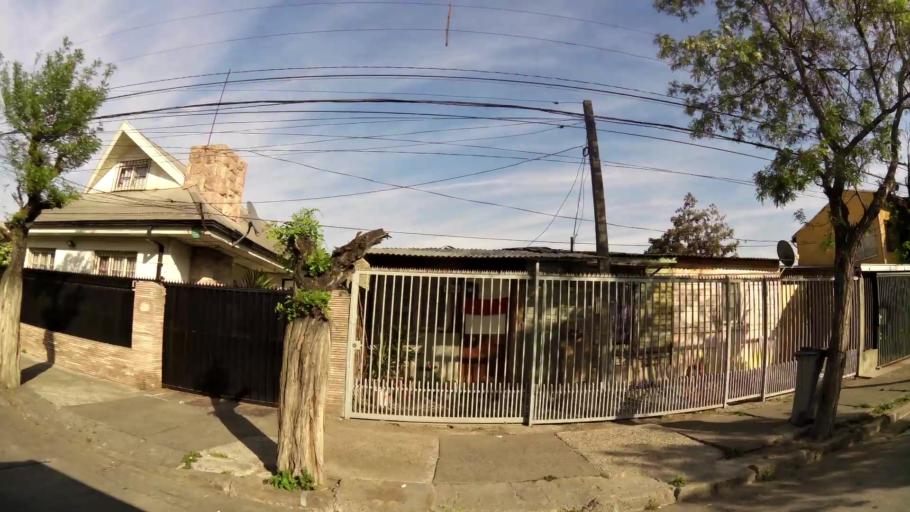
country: CL
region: Santiago Metropolitan
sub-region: Provincia de Santiago
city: Santiago
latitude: -33.5104
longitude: -70.6680
